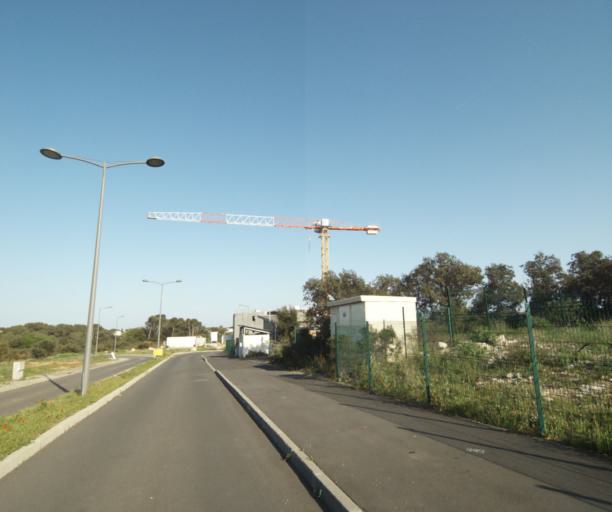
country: FR
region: Languedoc-Roussillon
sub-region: Departement de l'Herault
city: Le Cres
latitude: 43.6485
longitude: 3.9239
